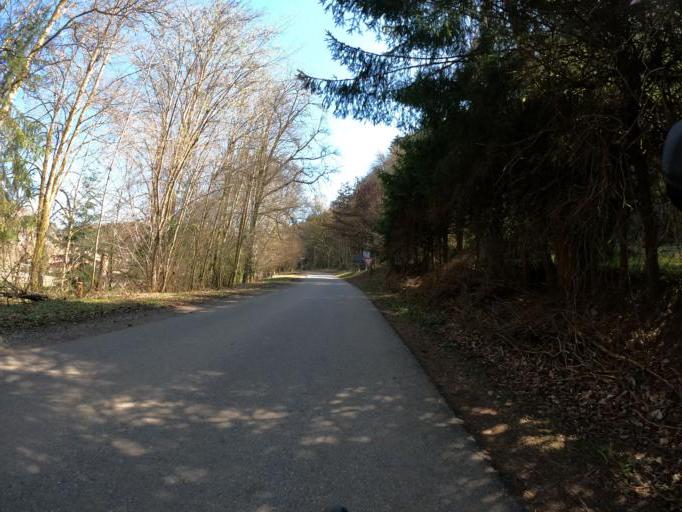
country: DE
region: Baden-Wuerttemberg
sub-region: Tuebingen Region
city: Haigerloch
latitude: 48.4029
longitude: 8.7684
